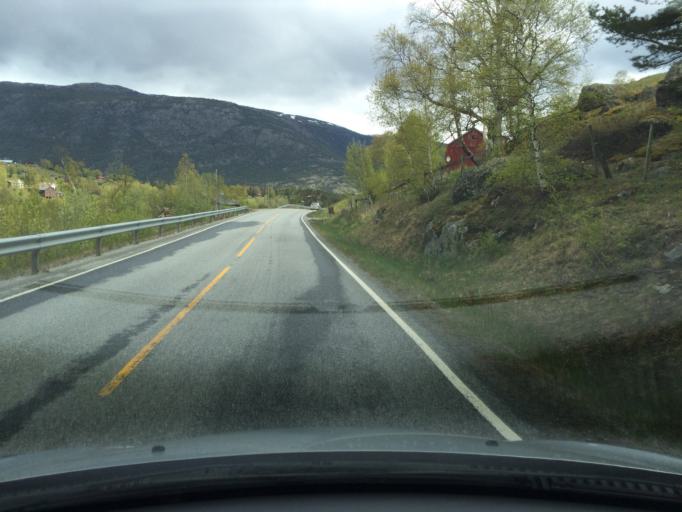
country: NO
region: Oppland
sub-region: Lom
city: Fossbergom
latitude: 61.8292
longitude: 8.5510
